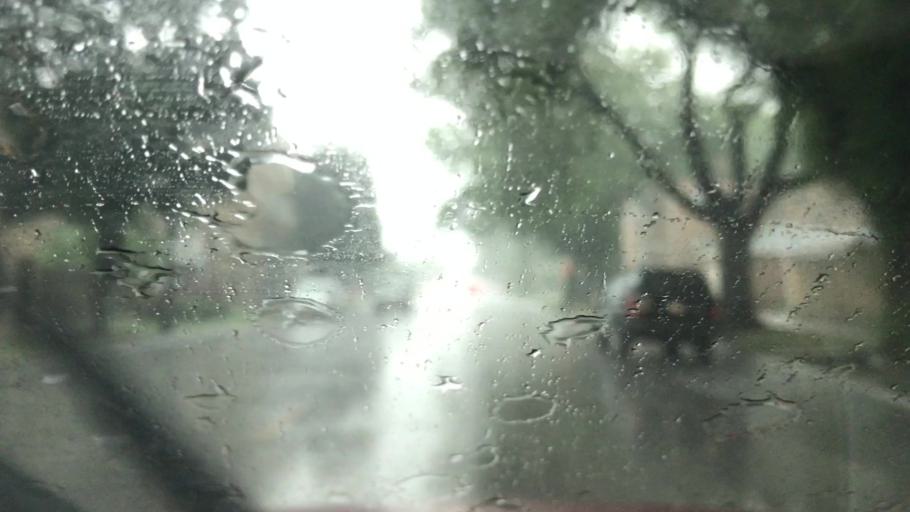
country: US
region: Illinois
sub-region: Cook County
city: Cicero
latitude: 41.8740
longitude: -87.7549
